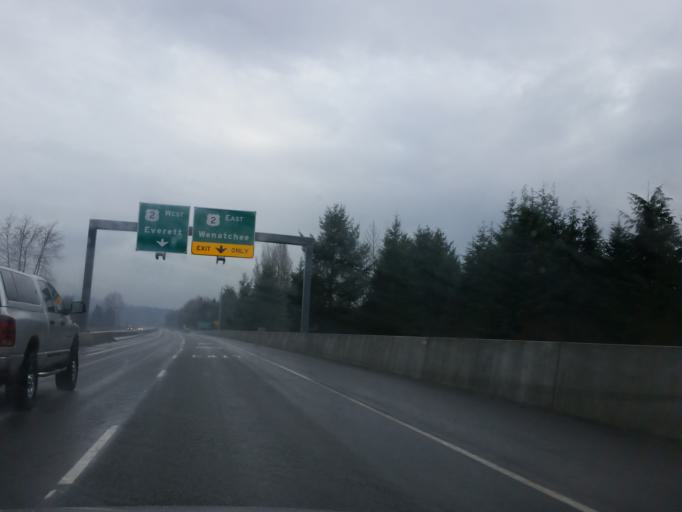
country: US
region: Washington
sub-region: Snohomish County
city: Monroe
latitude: 47.8532
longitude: -121.9976
